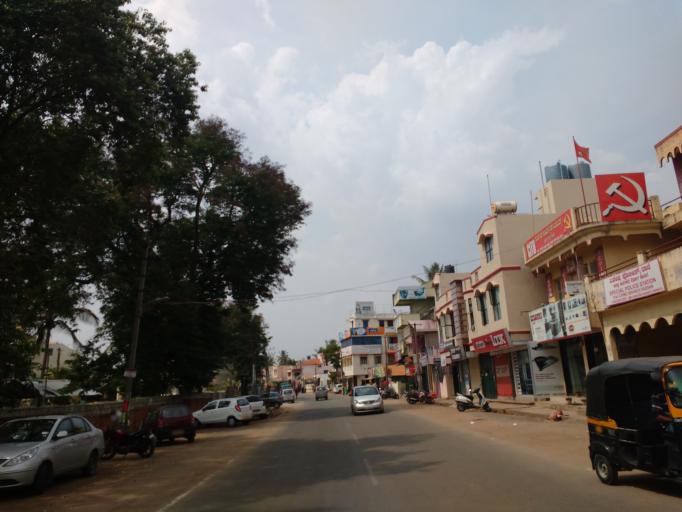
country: IN
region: Karnataka
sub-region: Hassan
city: Hassan
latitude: 13.0116
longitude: 76.1030
